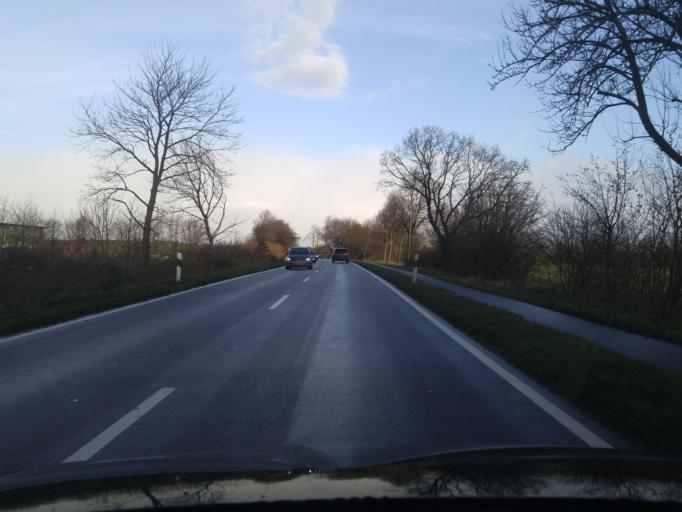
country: DE
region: Schleswig-Holstein
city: Timmendorfer Strand
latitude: 53.9755
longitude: 10.7725
